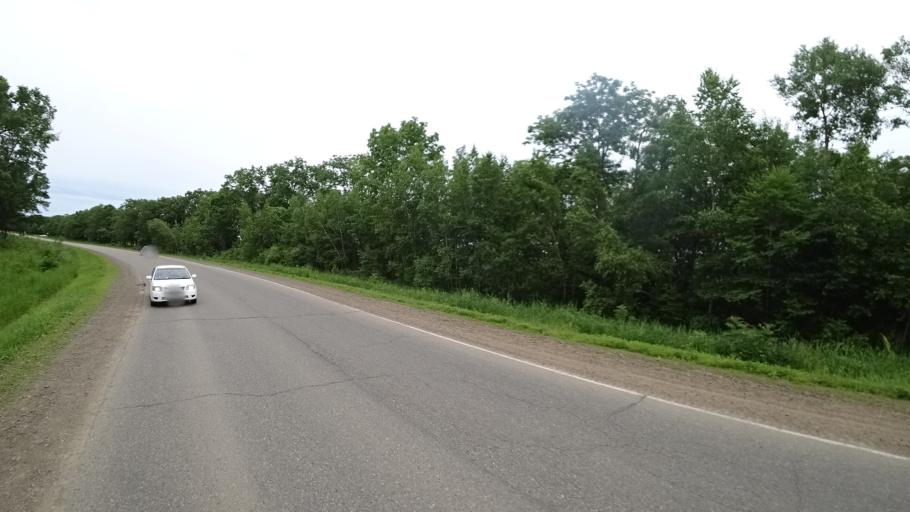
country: RU
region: Primorskiy
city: Novosysoyevka
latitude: 44.1885
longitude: 133.3547
